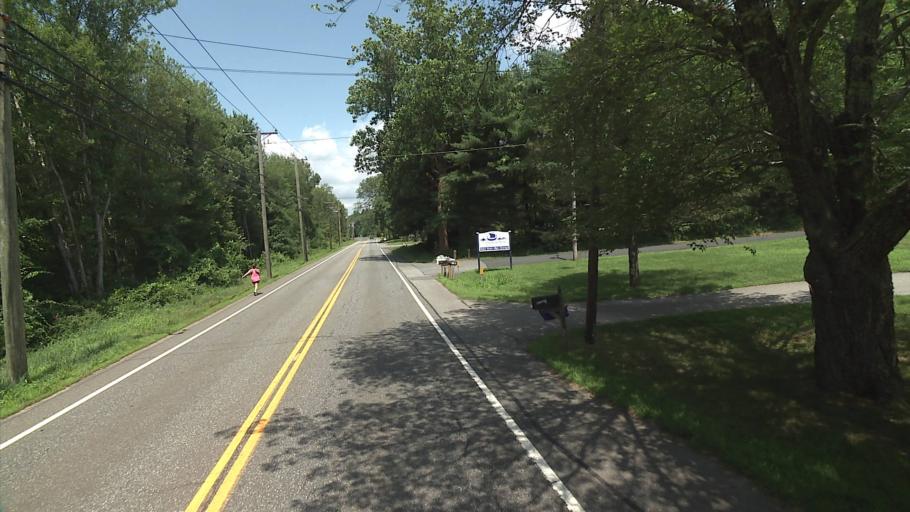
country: US
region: Connecticut
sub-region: Middlesex County
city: Chester Center
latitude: 41.4233
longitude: -72.4469
